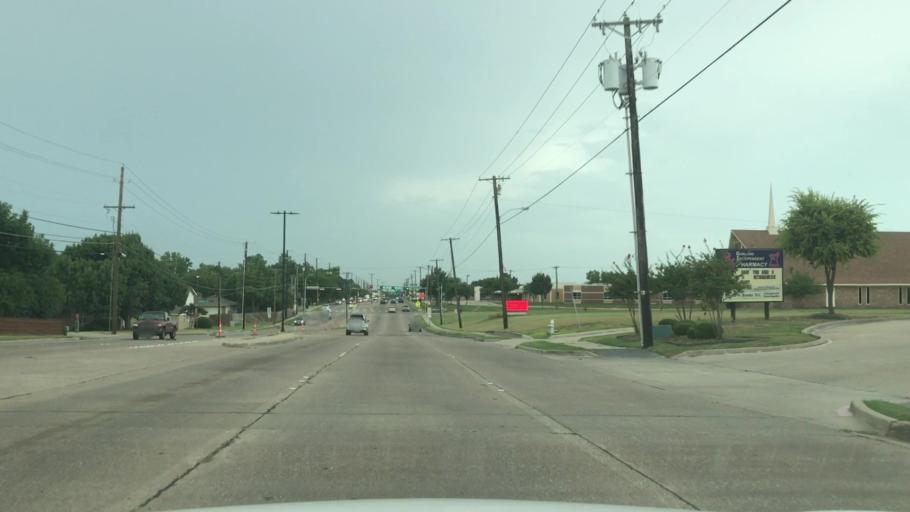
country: US
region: Texas
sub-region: Dallas County
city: Garland
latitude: 32.8703
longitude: -96.6117
